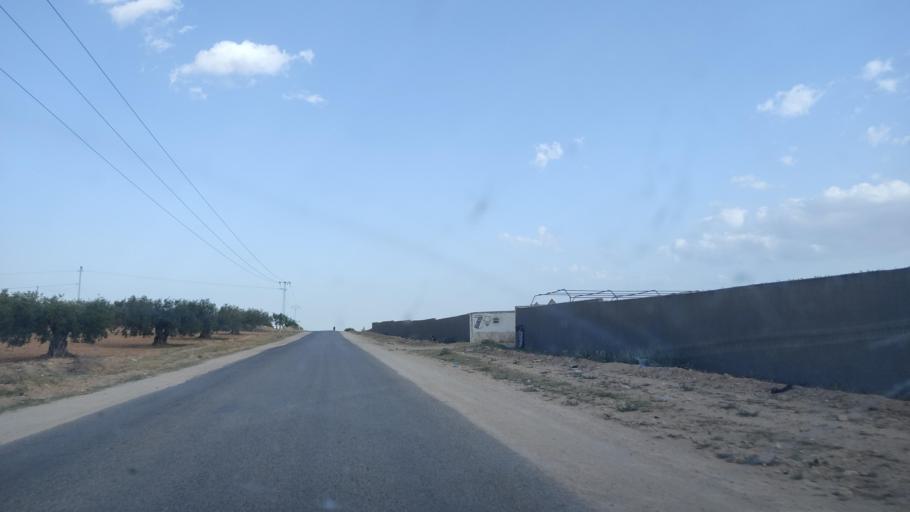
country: TN
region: Safaqis
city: Sfax
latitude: 34.8413
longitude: 10.6230
